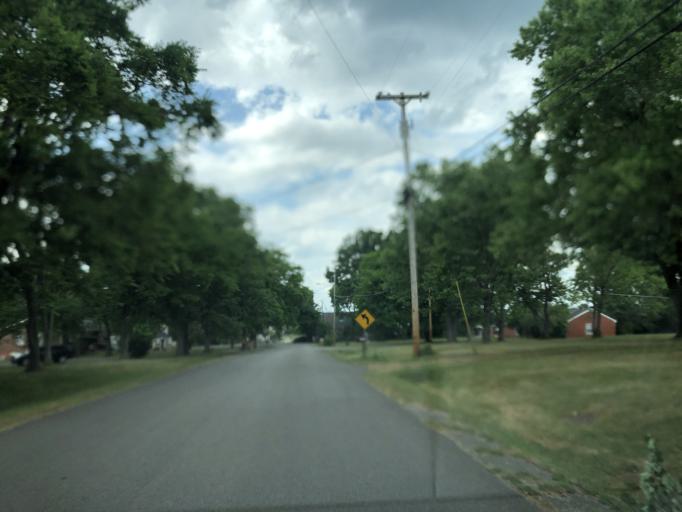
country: US
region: Tennessee
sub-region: Davidson County
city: Goodlettsville
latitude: 36.2782
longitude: -86.6988
